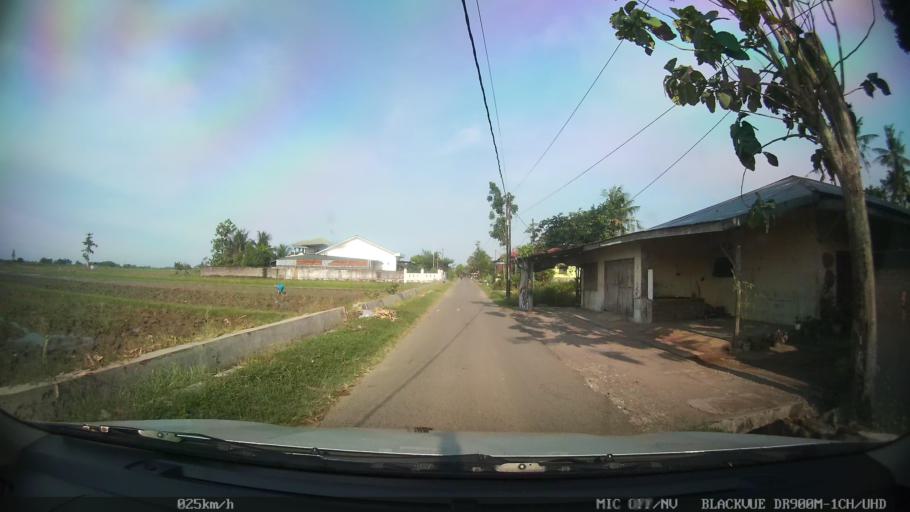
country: ID
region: North Sumatra
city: Binjai
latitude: 3.6210
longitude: 98.5240
